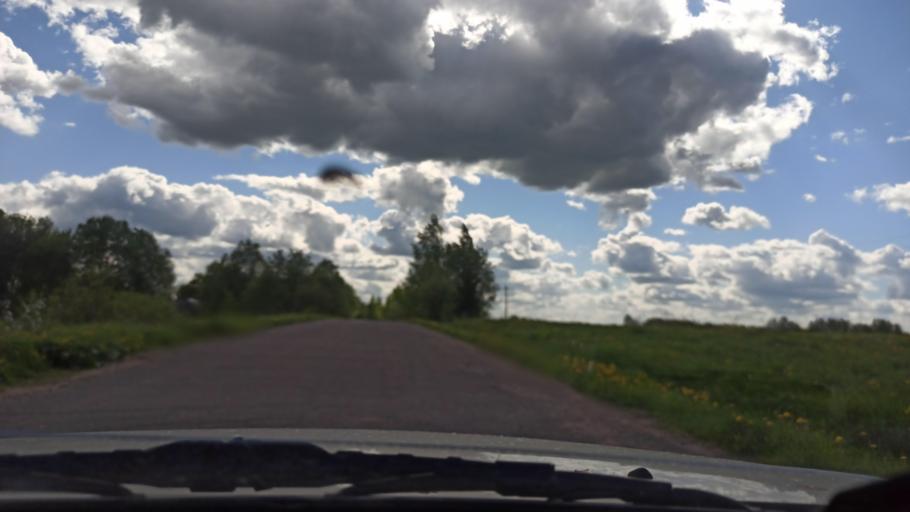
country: RU
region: Vologda
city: Molochnoye
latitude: 59.3745
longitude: 39.7081
